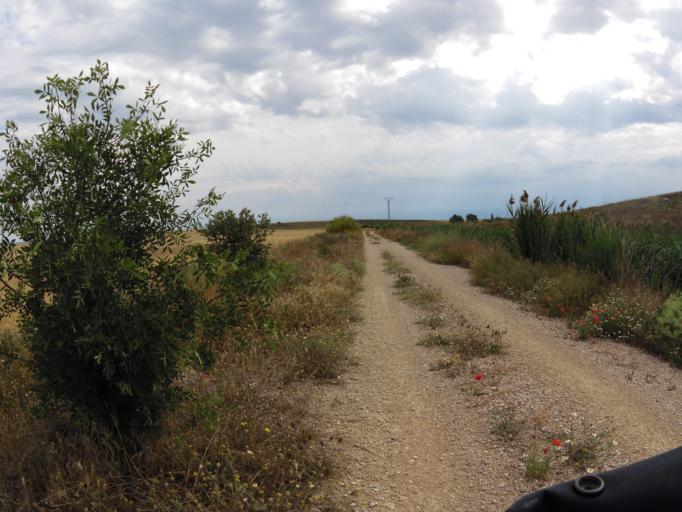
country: ES
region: Castille-La Mancha
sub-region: Provincia de Albacete
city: Albacete
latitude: 39.0404
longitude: -1.7802
